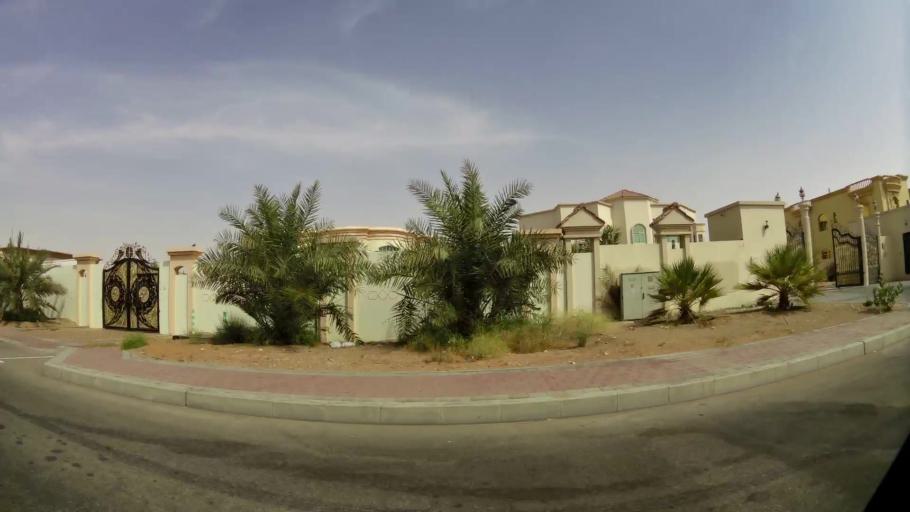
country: AE
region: Abu Dhabi
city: Al Ain
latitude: 24.1683
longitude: 55.6955
